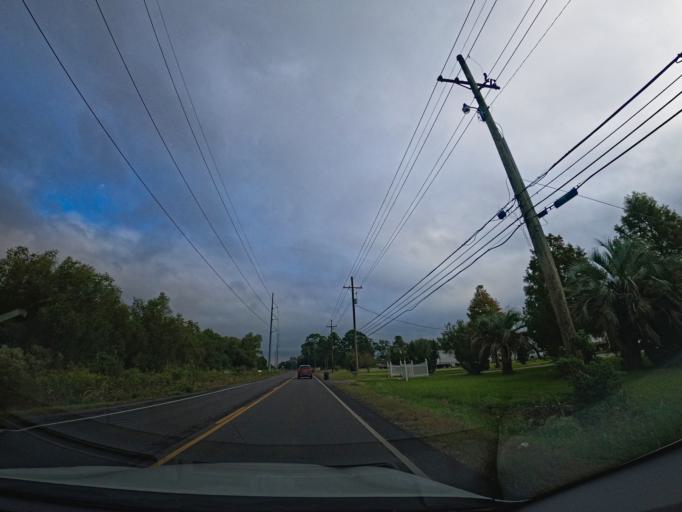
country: US
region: Louisiana
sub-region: Terrebonne Parish
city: Presquille
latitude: 29.5268
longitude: -90.6747
